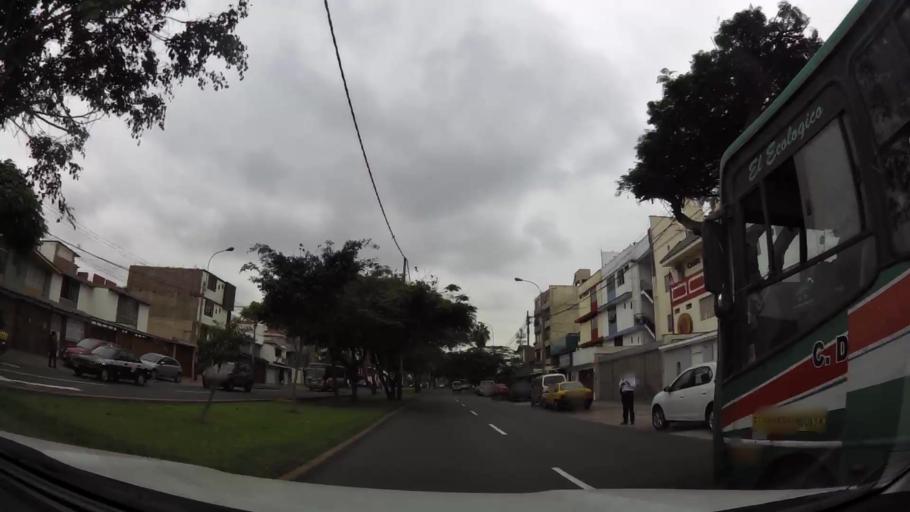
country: PE
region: Lima
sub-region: Lima
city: Surco
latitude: -12.1355
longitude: -76.9838
